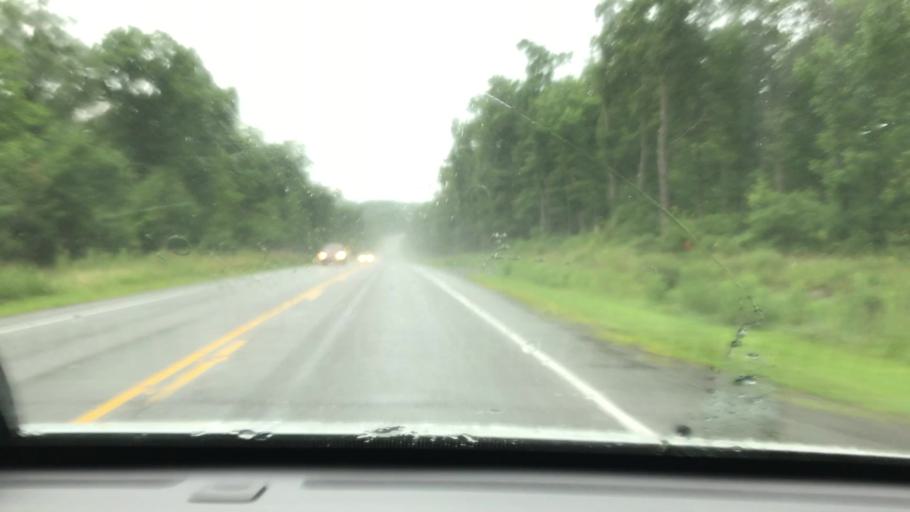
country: US
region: Pennsylvania
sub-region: Clearfield County
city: Osceola Mills
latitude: 40.8238
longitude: -78.2249
